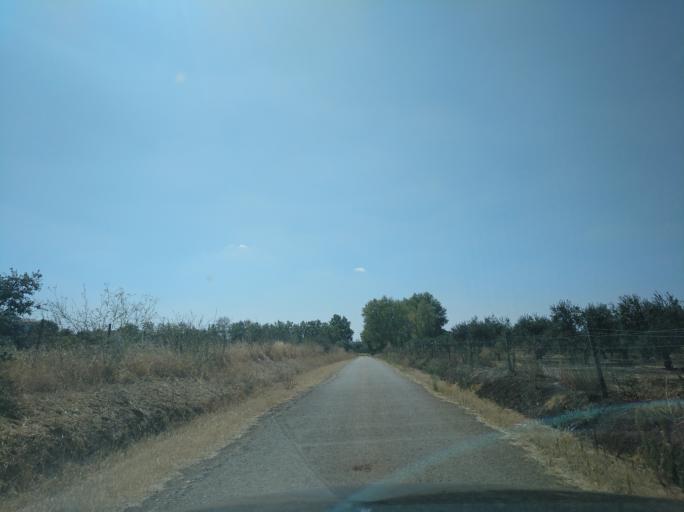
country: PT
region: Portalegre
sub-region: Campo Maior
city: Campo Maior
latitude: 39.0246
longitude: -7.0965
